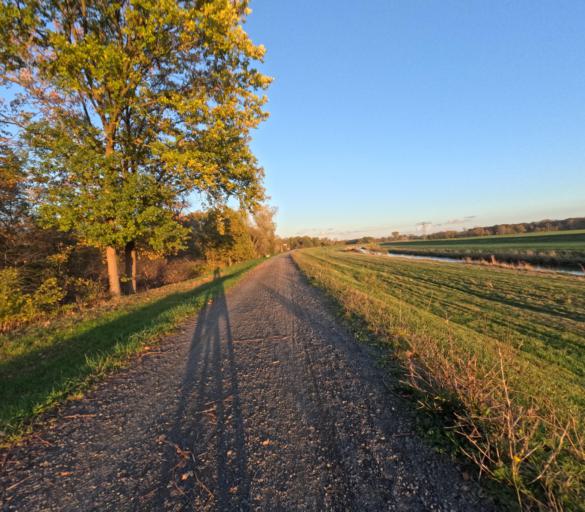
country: DE
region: Saxony
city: Schkeuditz
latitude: 51.3817
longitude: 12.2571
